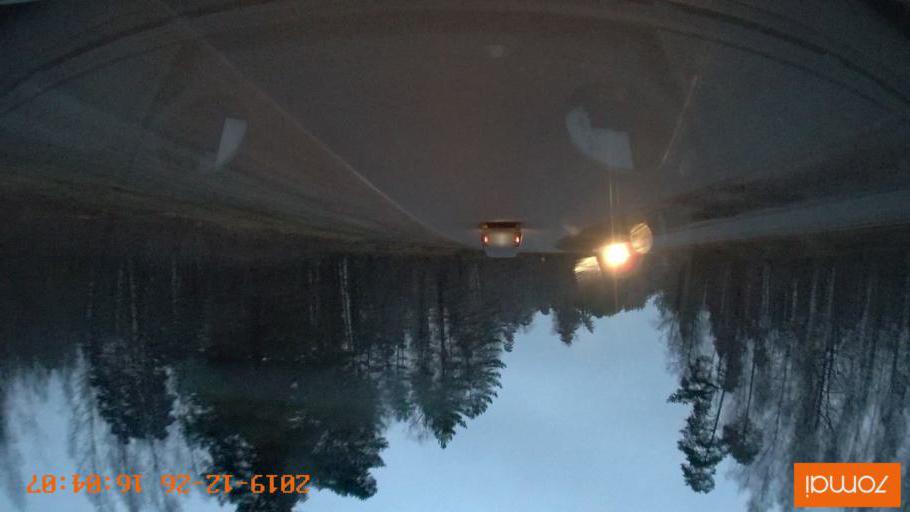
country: RU
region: Jaroslavl
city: Rybinsk
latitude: 58.0088
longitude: 38.8628
